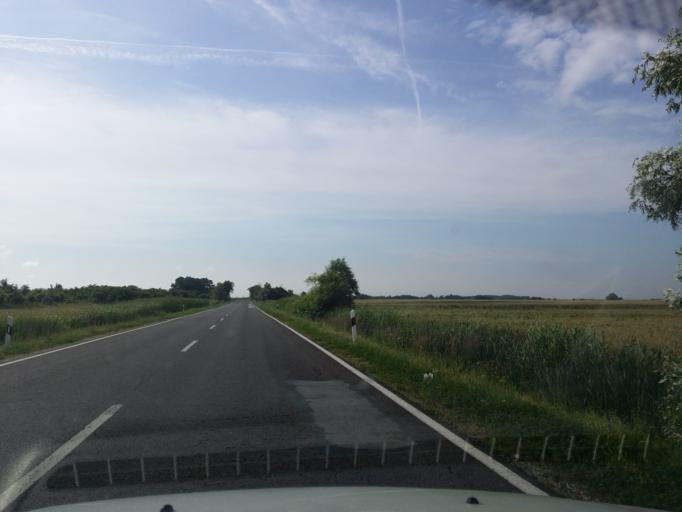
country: HU
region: Hajdu-Bihar
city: Egyek
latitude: 47.5530
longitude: 20.8768
